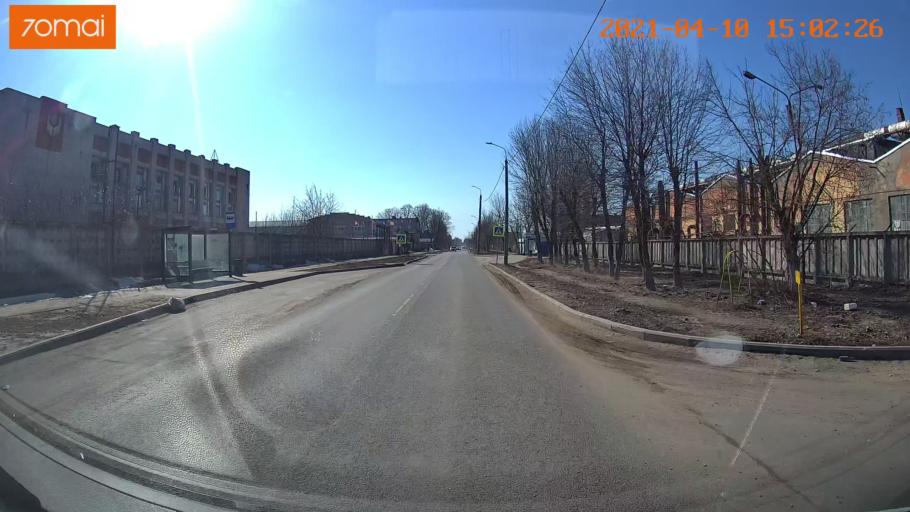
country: RU
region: Ivanovo
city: Bogorodskoye
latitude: 56.9961
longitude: 41.0443
